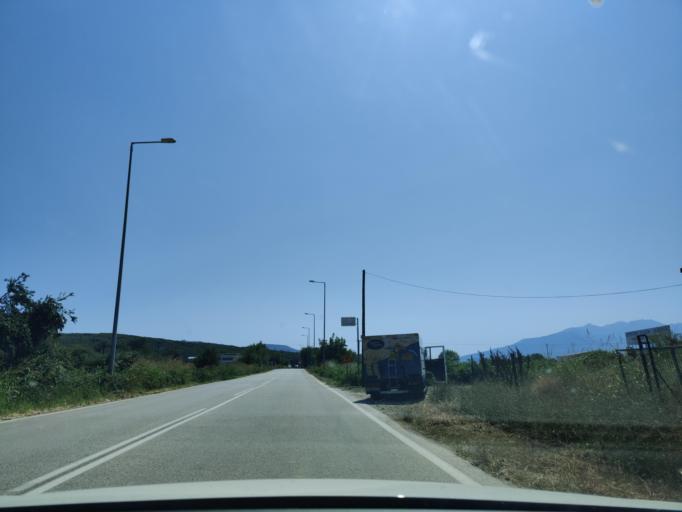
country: GR
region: East Macedonia and Thrace
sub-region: Nomos Kavalas
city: Amygdaleonas
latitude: 40.9796
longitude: 24.3661
